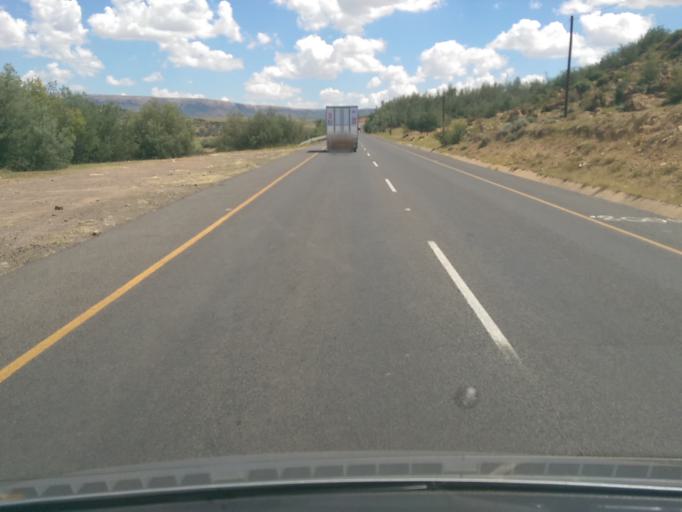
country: LS
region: Maseru
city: Maseru
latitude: -29.3977
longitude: 27.5354
